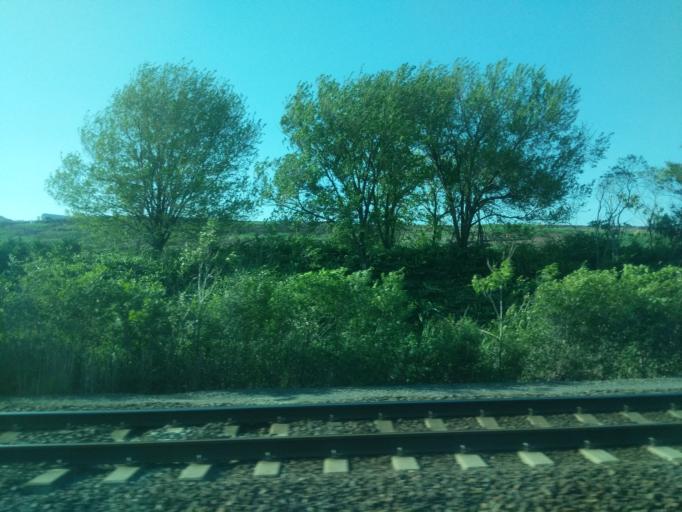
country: US
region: New Jersey
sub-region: Hudson County
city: Harrison
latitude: 40.7440
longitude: -74.1268
